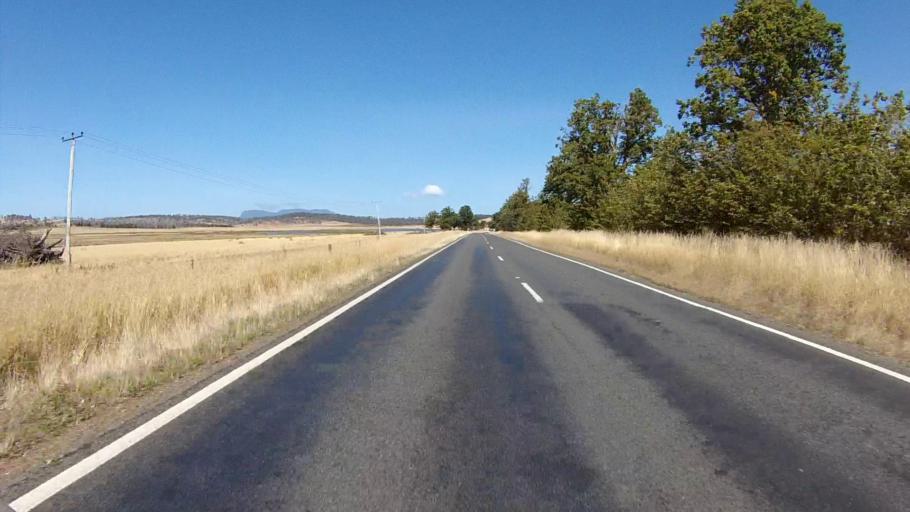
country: AU
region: Tasmania
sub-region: Sorell
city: Sorell
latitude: -42.4774
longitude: 147.9303
